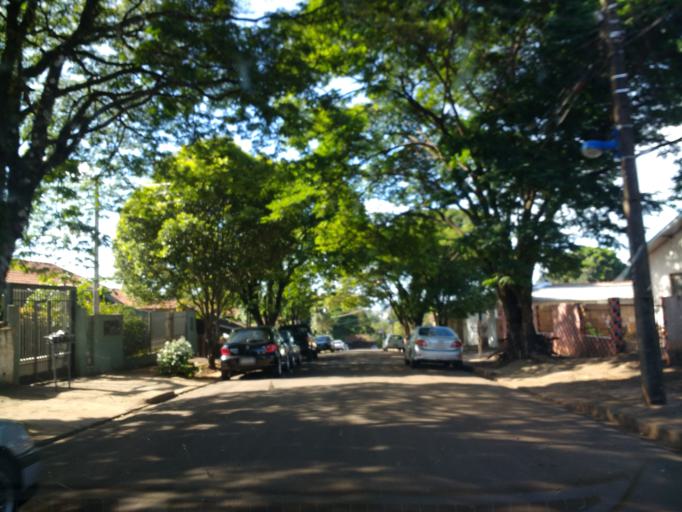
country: BR
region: Parana
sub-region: Maringa
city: Maringa
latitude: -23.4166
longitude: -51.9775
